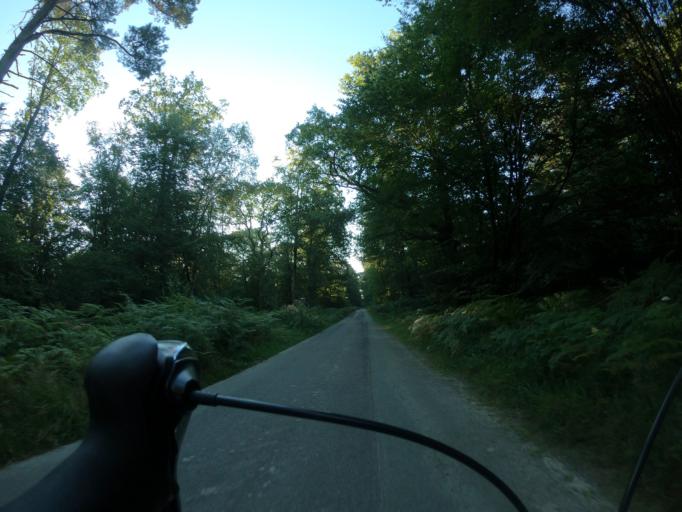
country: FR
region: Lower Normandy
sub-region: Departement de l'Orne
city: Magny-le-Desert
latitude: 48.5407
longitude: -0.3365
